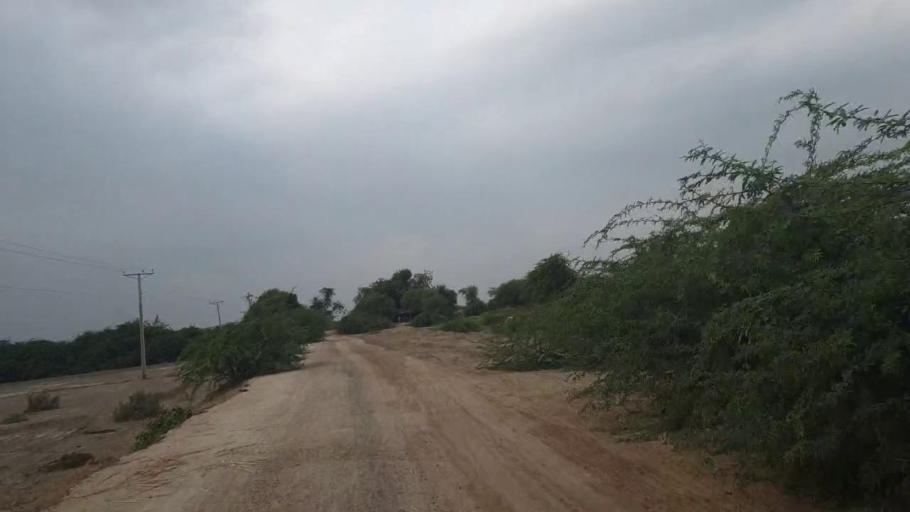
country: PK
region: Sindh
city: Badin
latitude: 24.6159
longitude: 68.6818
